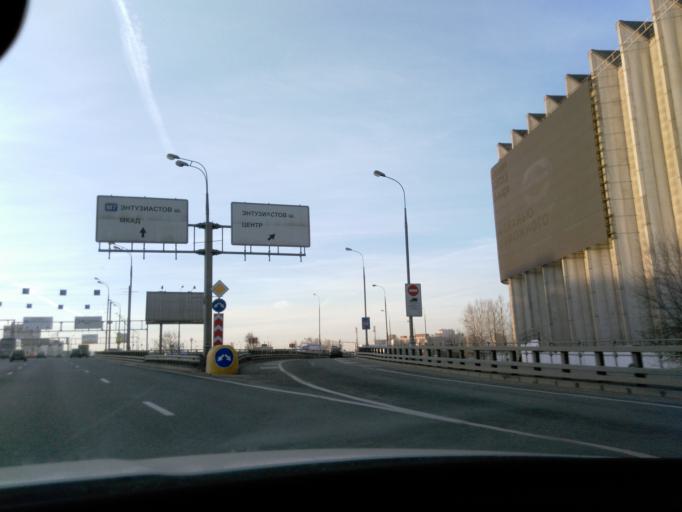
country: RU
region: Moscow
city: Lefortovo
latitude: 55.7500
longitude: 37.6975
